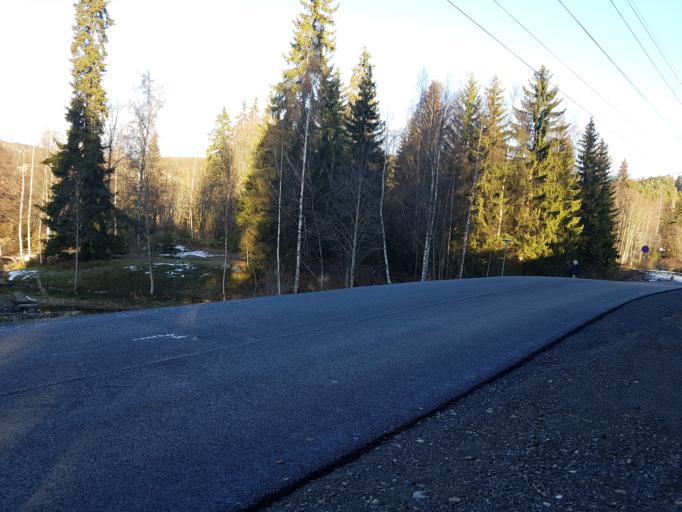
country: NO
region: Oppland
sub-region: Lillehammer
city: Lillehammer
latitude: 61.1183
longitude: 10.4763
